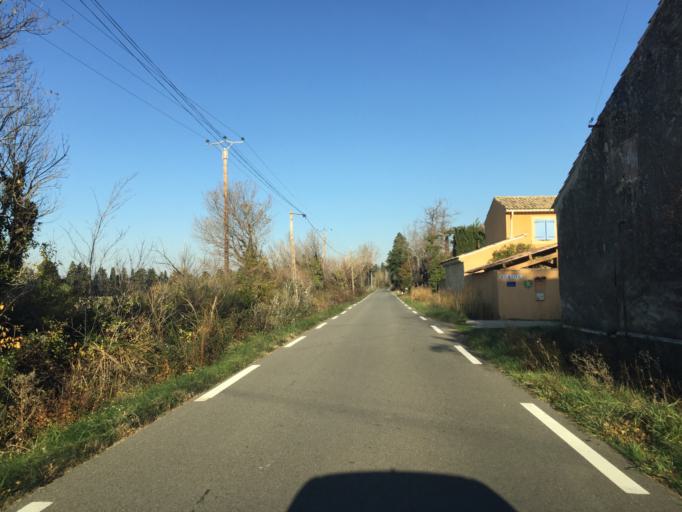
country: FR
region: Provence-Alpes-Cote d'Azur
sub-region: Departement du Vaucluse
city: Camaret-sur-Aigues
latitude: 44.1897
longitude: 4.8968
